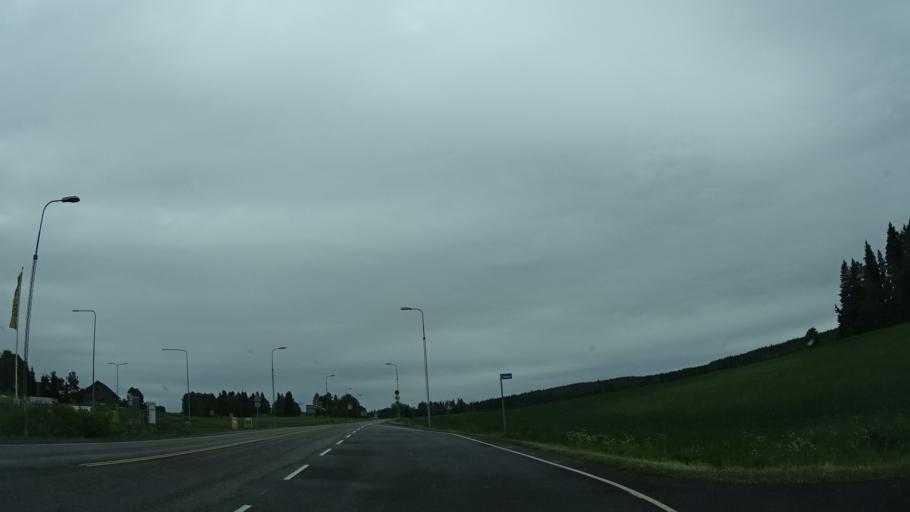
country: FI
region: Varsinais-Suomi
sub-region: Salo
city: Pernioe
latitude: 60.2048
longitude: 23.1119
